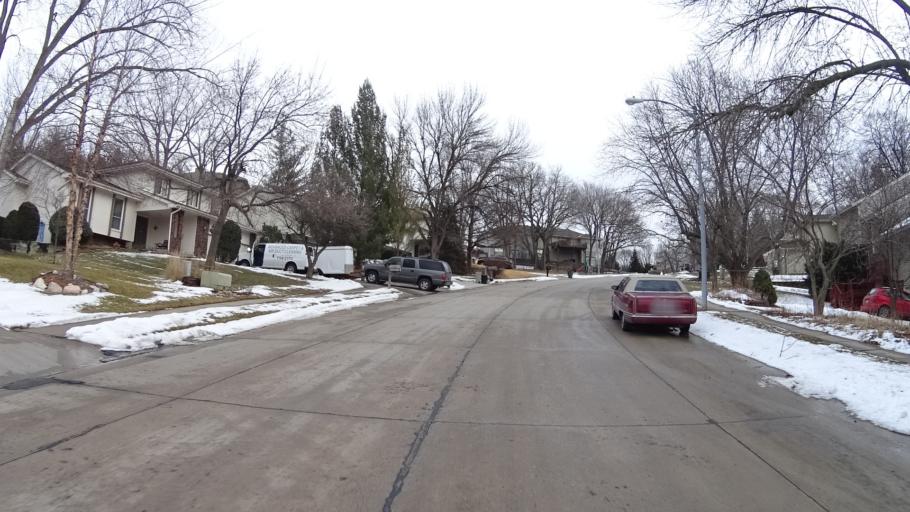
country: US
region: Nebraska
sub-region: Sarpy County
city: Bellevue
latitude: 41.1755
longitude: -95.9127
